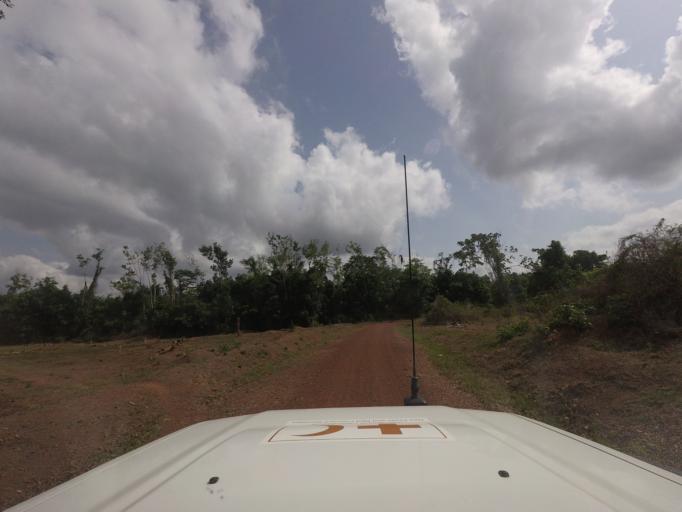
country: LR
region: Nimba
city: Sanniquellie
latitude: 7.1730
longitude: -9.0859
